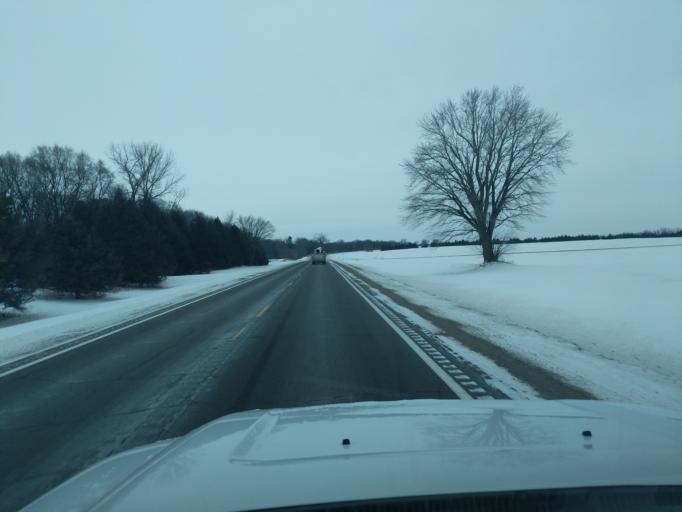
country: US
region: Minnesota
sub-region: Redwood County
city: Redwood Falls
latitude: 44.5732
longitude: -94.9946
